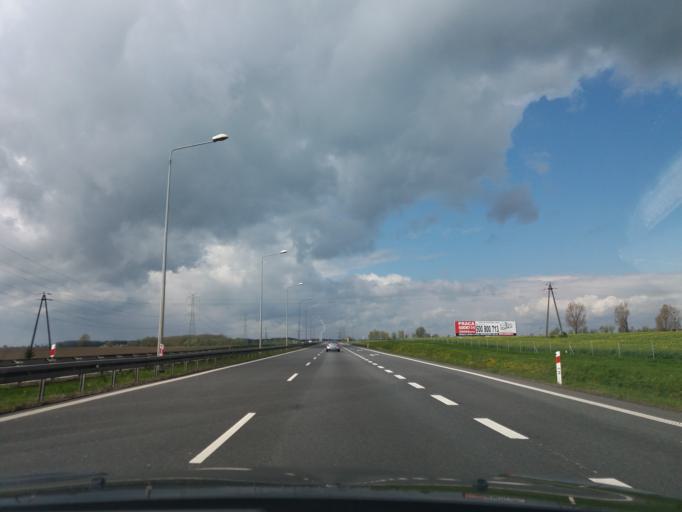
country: PL
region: Opole Voivodeship
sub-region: Powiat brzeski
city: Olszanka
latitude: 50.7529
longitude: 17.4379
